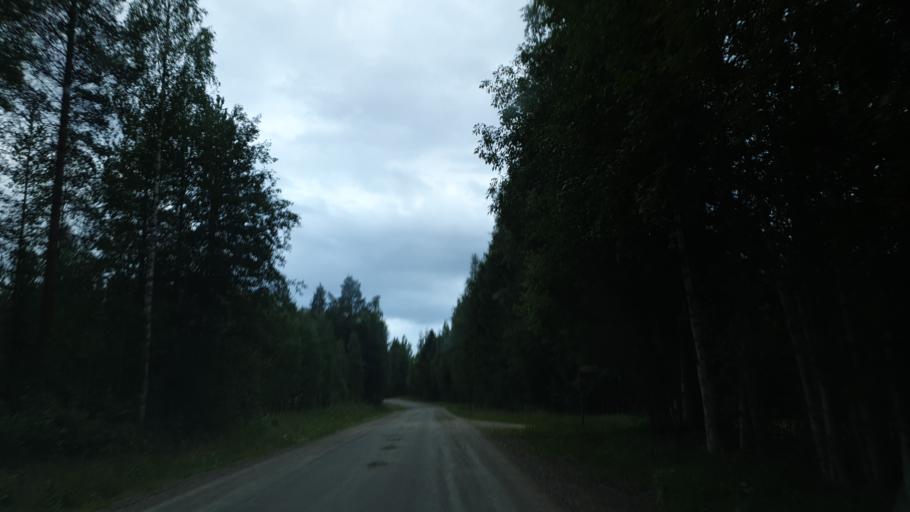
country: FI
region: Kainuu
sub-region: Kehys-Kainuu
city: Kuhmo
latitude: 64.1987
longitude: 29.3667
